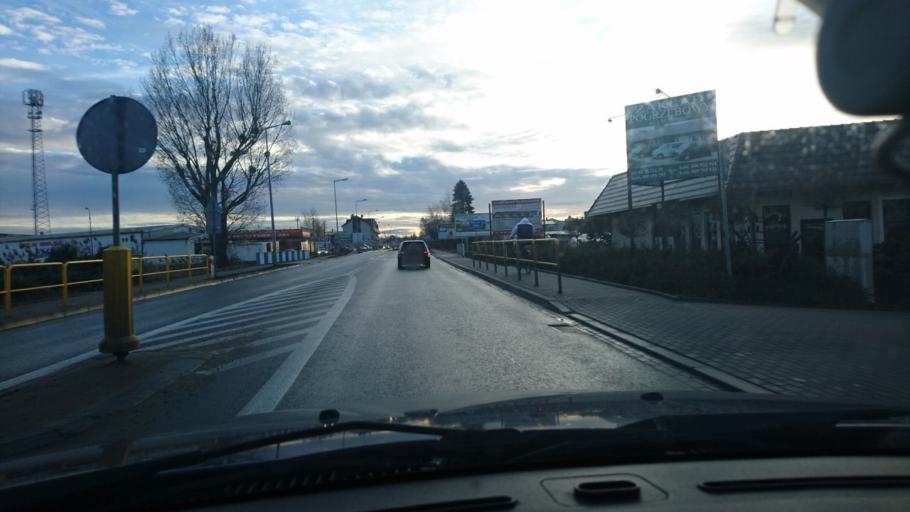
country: PL
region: Greater Poland Voivodeship
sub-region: Powiat kepinski
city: Kepno
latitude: 51.2809
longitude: 17.9921
